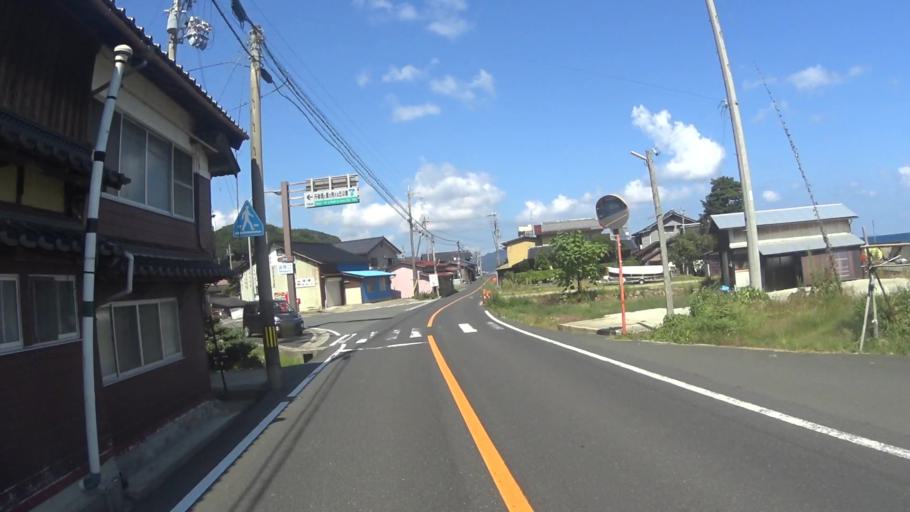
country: JP
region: Kyoto
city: Miyazu
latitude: 35.6244
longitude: 135.2451
